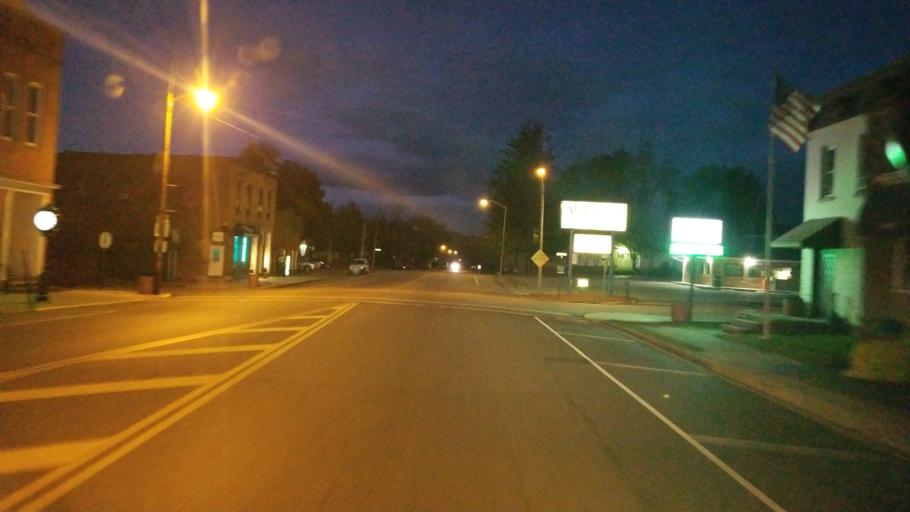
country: US
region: Ohio
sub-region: Vinton County
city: McArthur
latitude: 39.2468
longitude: -82.4798
